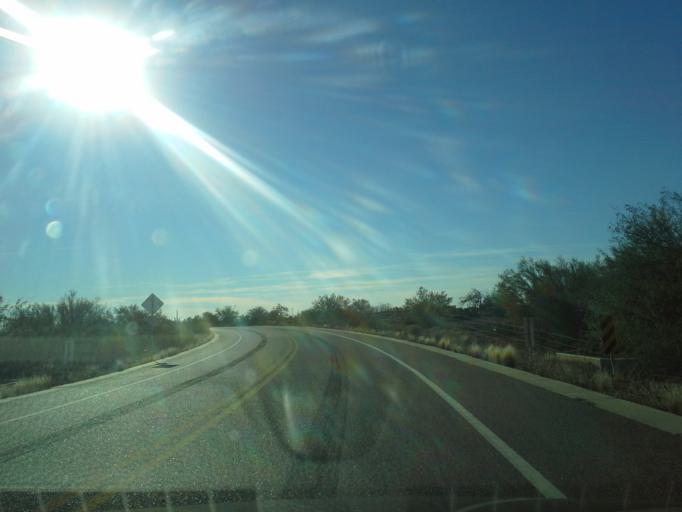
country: US
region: Arizona
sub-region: Pinal County
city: Gold Camp
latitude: 33.3027
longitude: -111.3747
